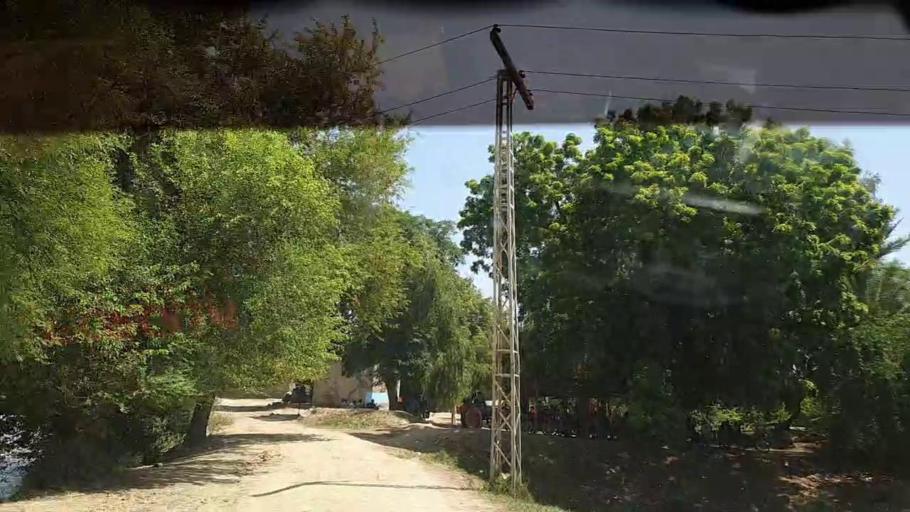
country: PK
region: Sindh
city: Ghauspur
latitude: 28.1639
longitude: 69.1361
